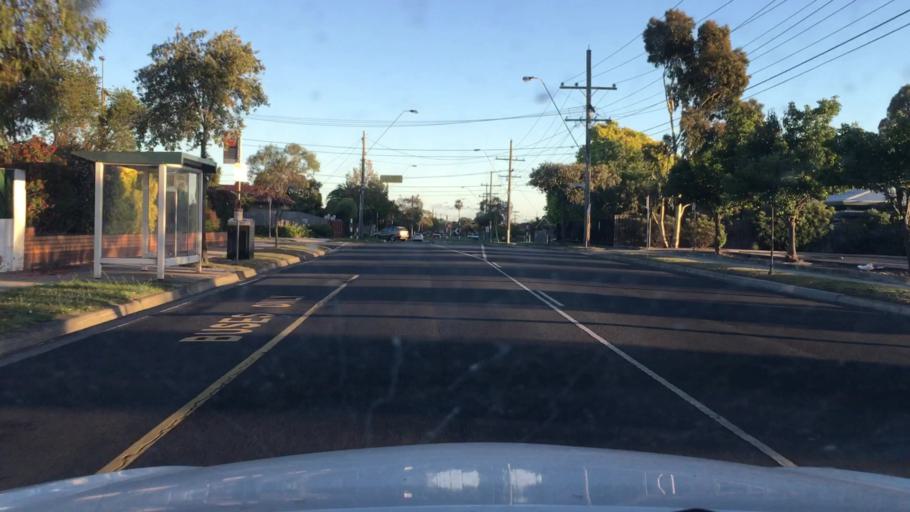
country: AU
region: Victoria
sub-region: Greater Dandenong
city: Keysborough
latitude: -37.9808
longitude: 145.1669
